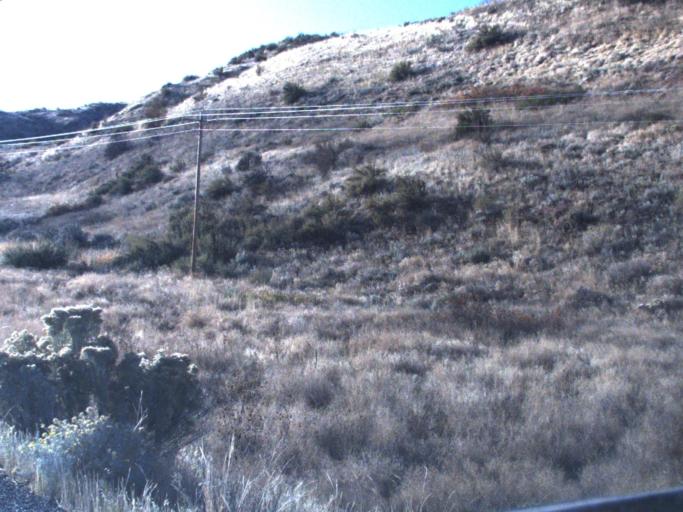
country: US
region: Washington
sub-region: Okanogan County
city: Coulee Dam
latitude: 47.9586
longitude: -118.6979
